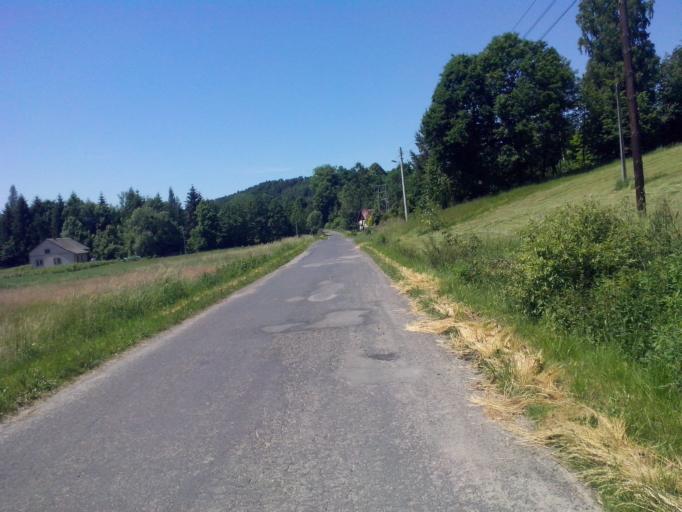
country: PL
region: Subcarpathian Voivodeship
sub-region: Powiat krosnienski
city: Leki
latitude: 49.8062
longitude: 21.6899
